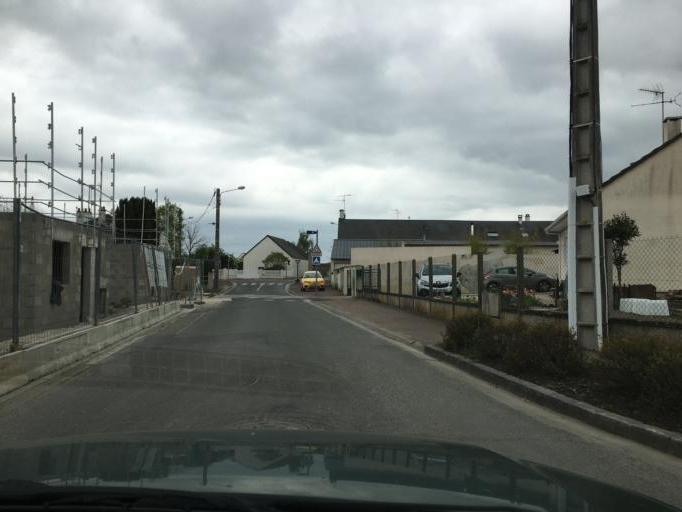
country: FR
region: Centre
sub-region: Departement du Loiret
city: Saint-Jean-de-la-Ruelle
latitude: 47.9220
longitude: 1.8711
